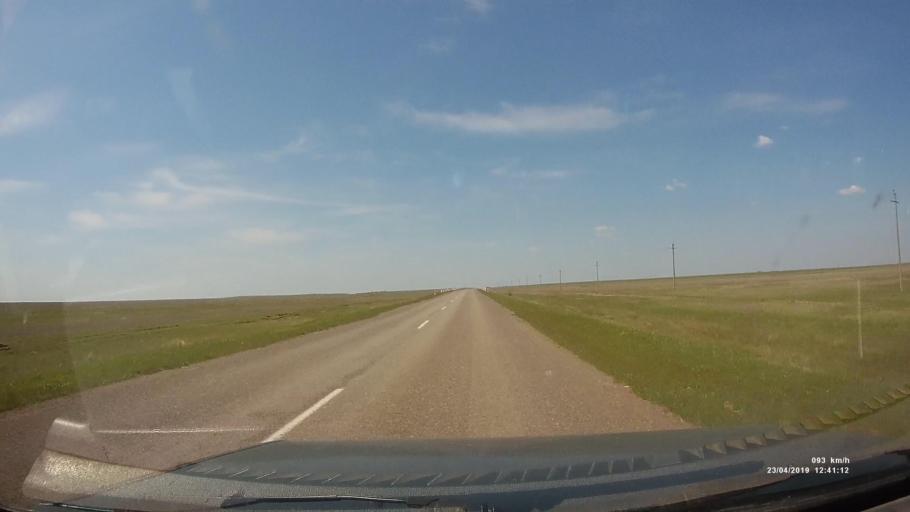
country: RU
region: Kalmykiya
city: Yashalta
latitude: 46.4463
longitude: 42.6846
